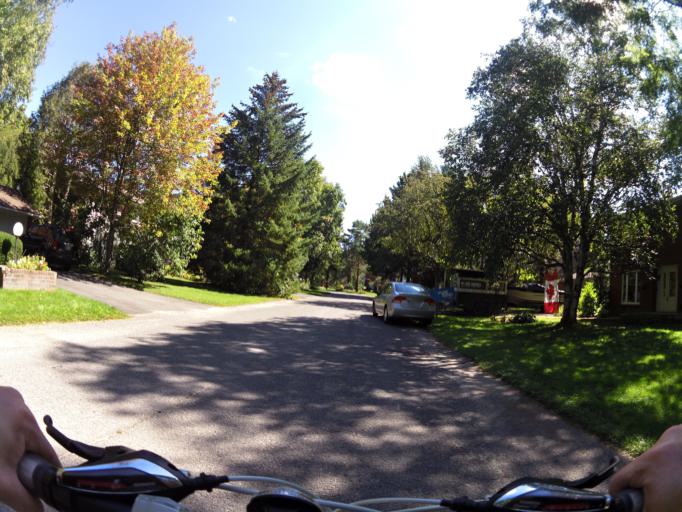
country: CA
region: Ontario
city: Bells Corners
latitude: 45.3262
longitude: -75.9014
